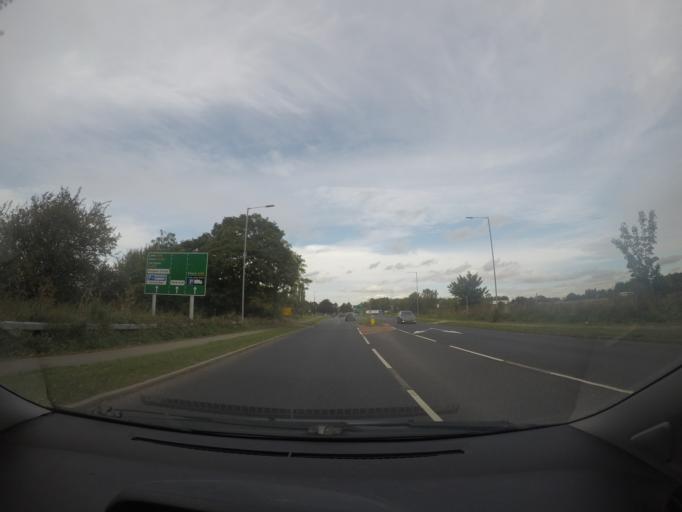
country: GB
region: England
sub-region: City of York
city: Fulford
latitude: 53.9225
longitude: -1.0651
